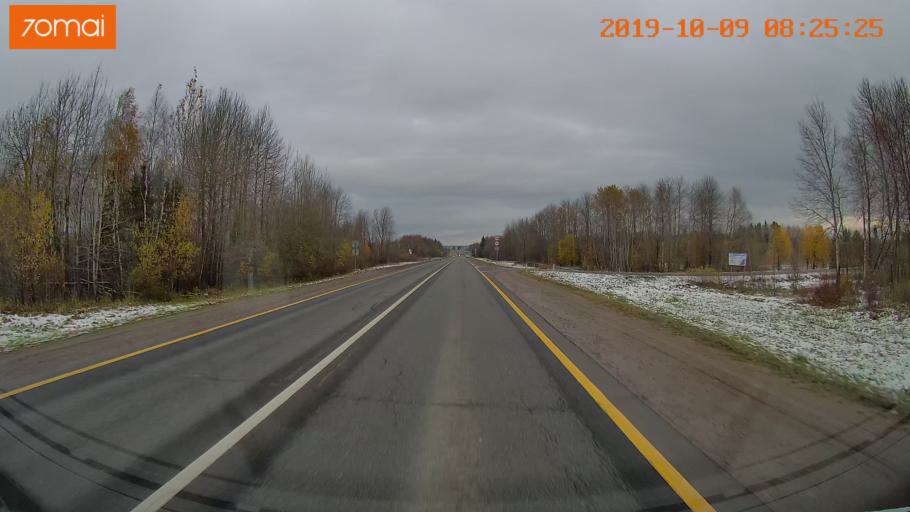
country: RU
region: Vologda
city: Gryazovets
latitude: 58.7809
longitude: 40.2724
